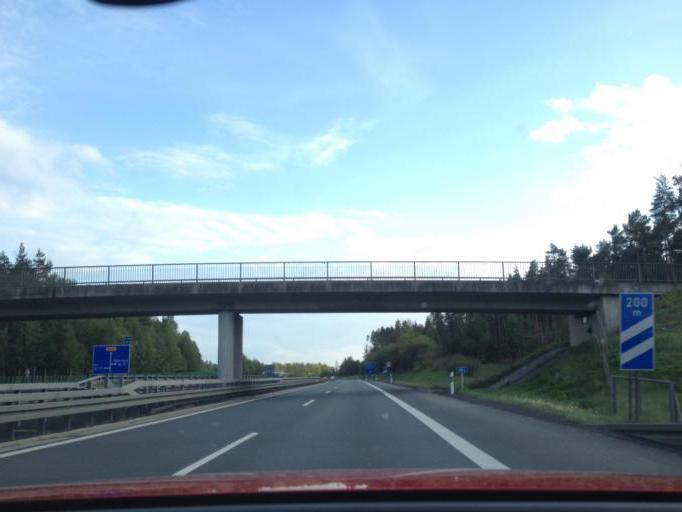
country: DE
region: Bavaria
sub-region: Upper Palatinate
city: Wiesau
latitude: 49.9167
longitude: 12.2210
